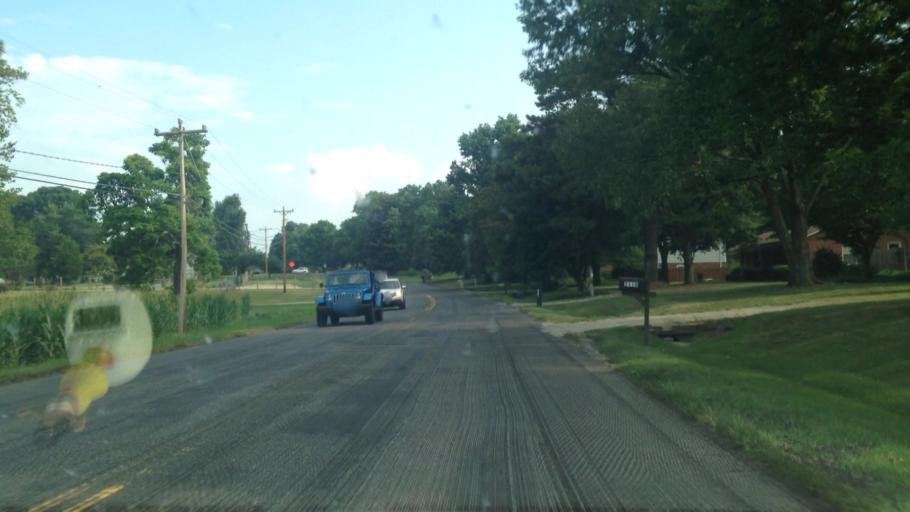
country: US
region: North Carolina
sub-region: Forsyth County
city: Kernersville
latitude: 36.0590
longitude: -80.0657
